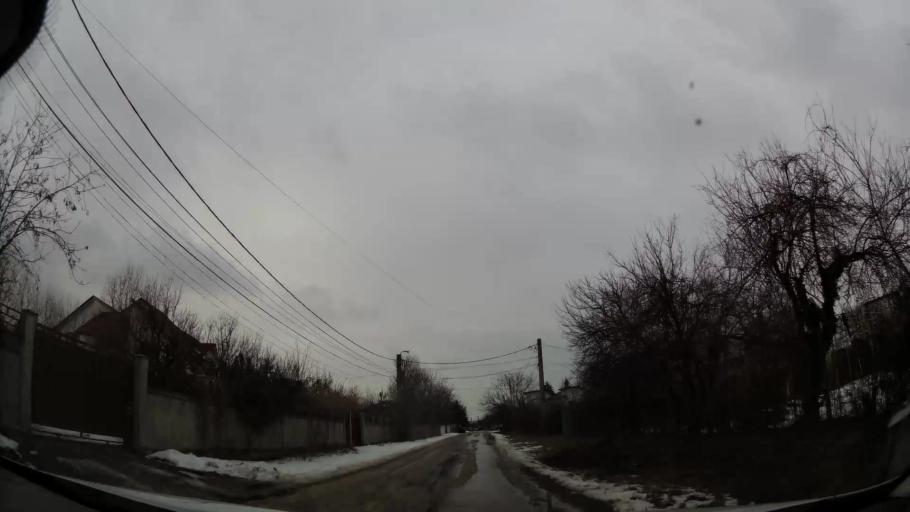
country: RO
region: Ilfov
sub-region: Comuna Tunari
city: Tunari
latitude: 44.5438
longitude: 26.1344
